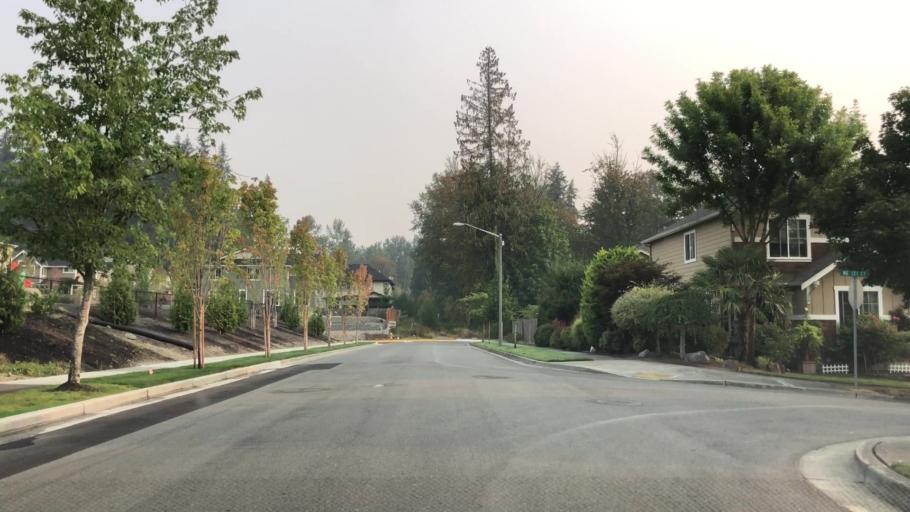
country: US
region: Washington
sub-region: King County
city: Redmond
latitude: 47.7083
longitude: -122.1053
